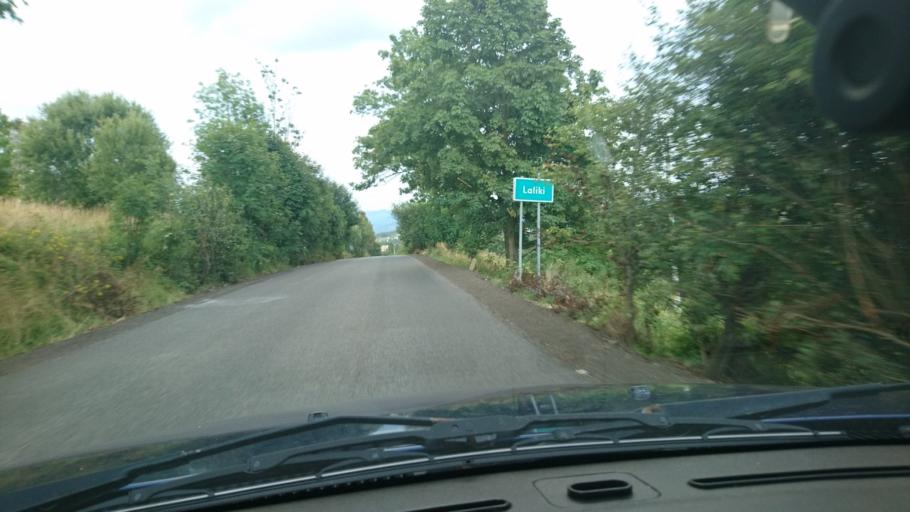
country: PL
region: Silesian Voivodeship
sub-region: Powiat zywiecki
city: Laliki
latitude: 49.5483
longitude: 19.0032
